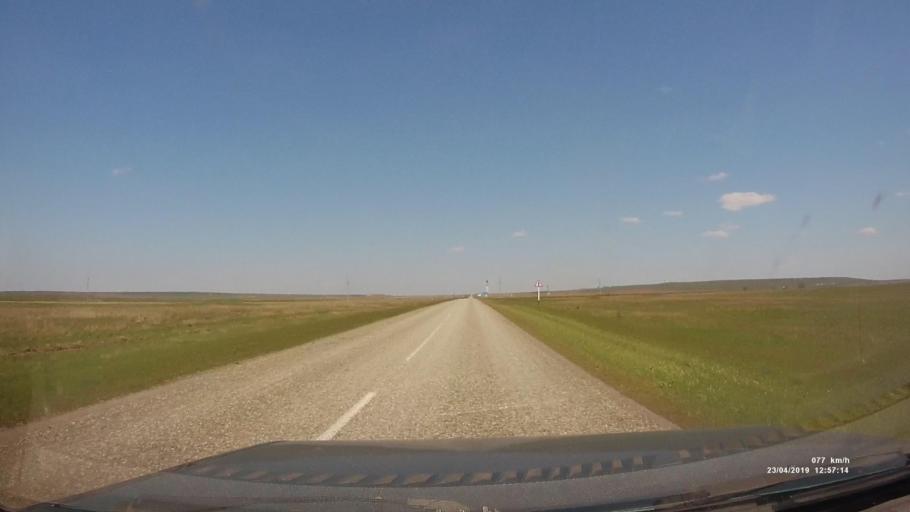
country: RU
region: Kalmykiya
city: Yashalta
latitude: 46.6019
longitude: 42.5794
